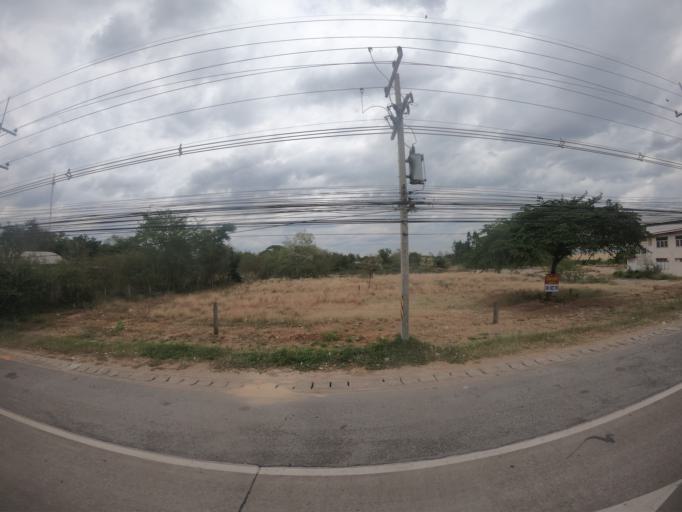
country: TH
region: Nakhon Ratchasima
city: Chok Chai
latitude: 14.7478
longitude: 102.1645
